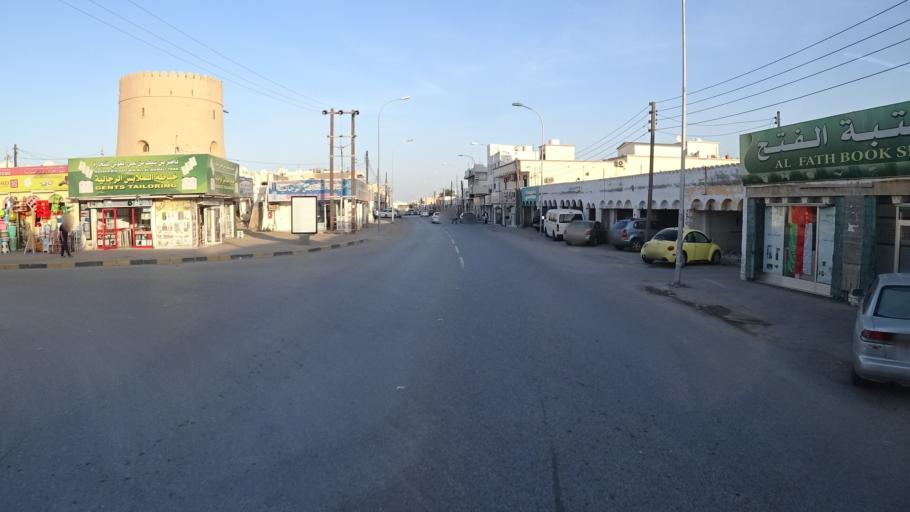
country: OM
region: Al Batinah
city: Barka'
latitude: 23.7074
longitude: 57.8932
